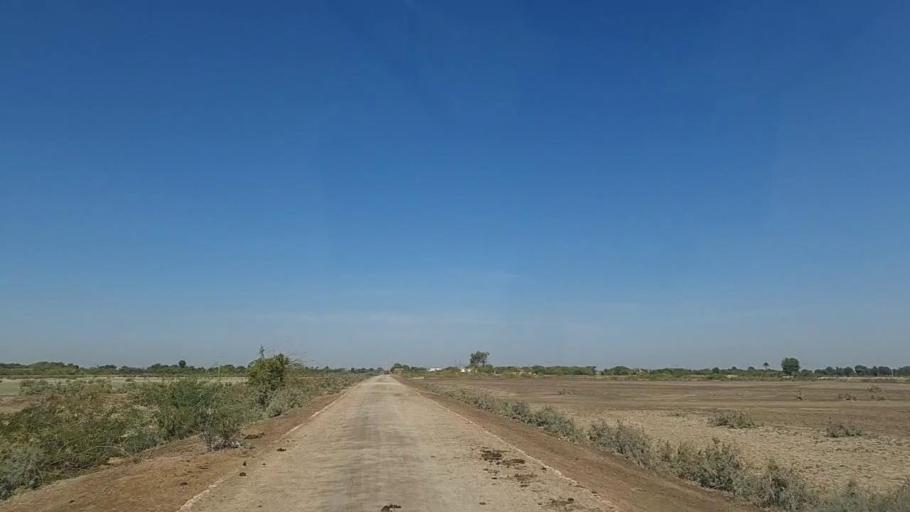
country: PK
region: Sindh
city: Samaro
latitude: 25.3053
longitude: 69.4858
